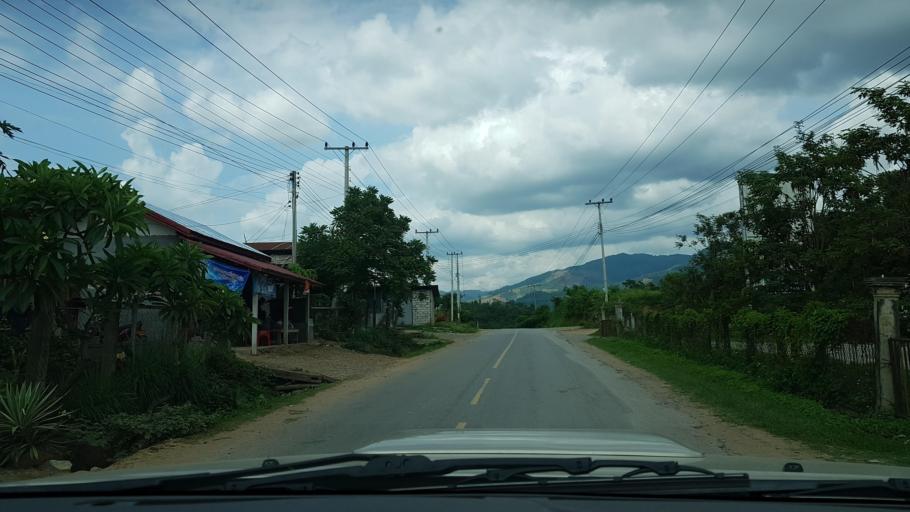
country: LA
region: Loungnamtha
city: Muang Nale
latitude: 20.1503
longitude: 101.4741
